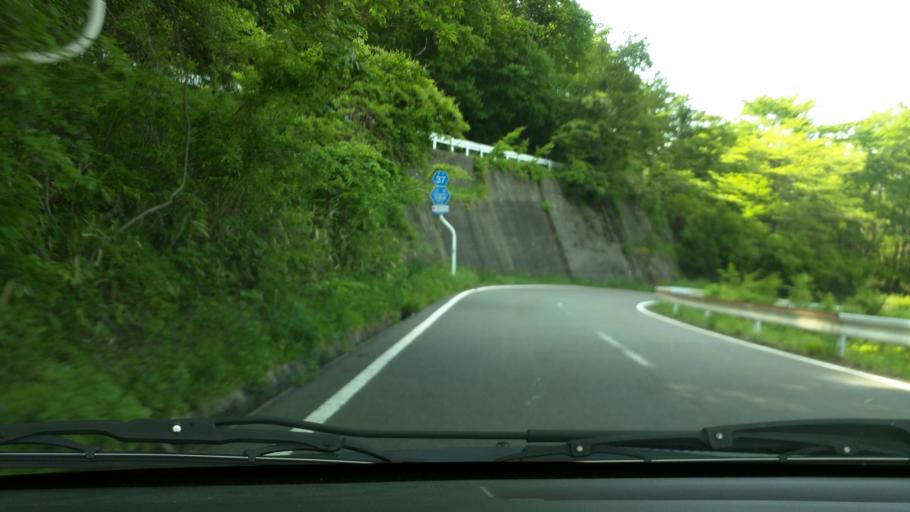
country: JP
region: Tochigi
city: Kuroiso
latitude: 37.2141
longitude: 140.0991
